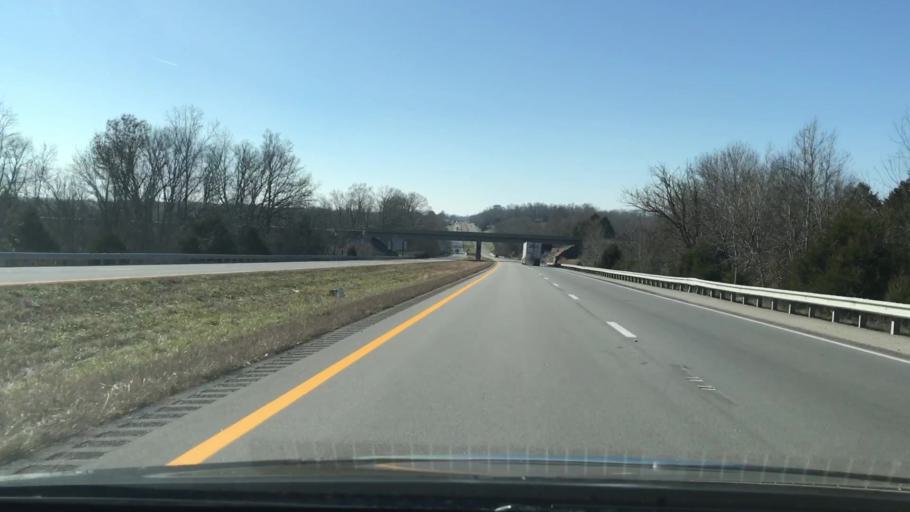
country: US
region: Kentucky
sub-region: Adair County
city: Columbia
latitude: 37.0849
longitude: -85.3095
